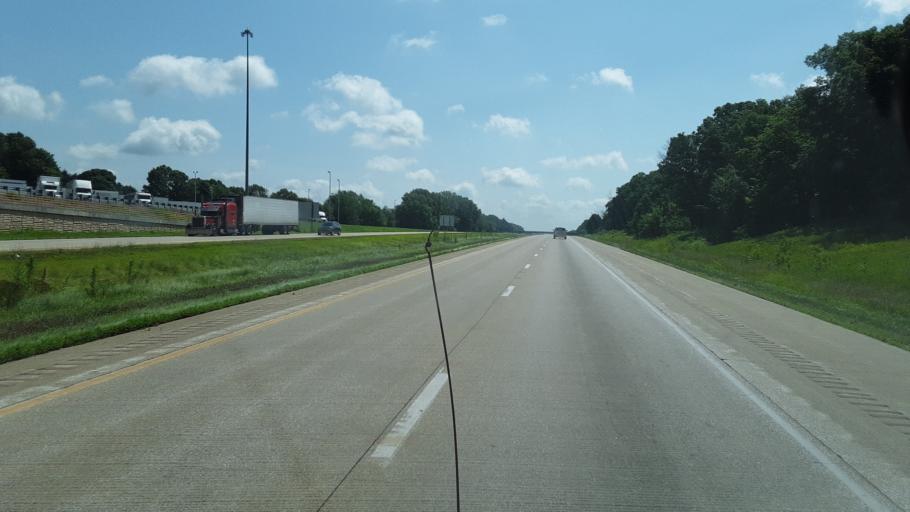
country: US
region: Illinois
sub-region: Clark County
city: Marshall
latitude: 39.4217
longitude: -87.6625
